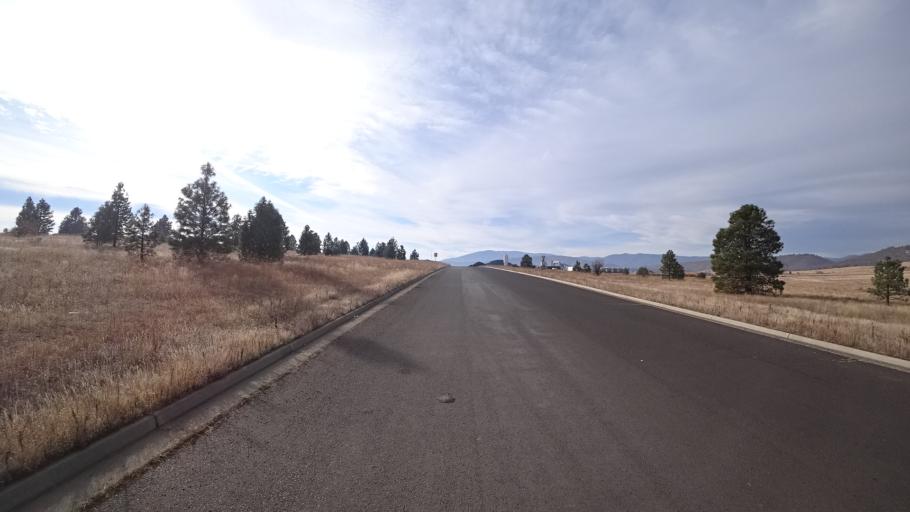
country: US
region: California
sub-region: Siskiyou County
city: Yreka
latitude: 41.7357
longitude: -122.5968
